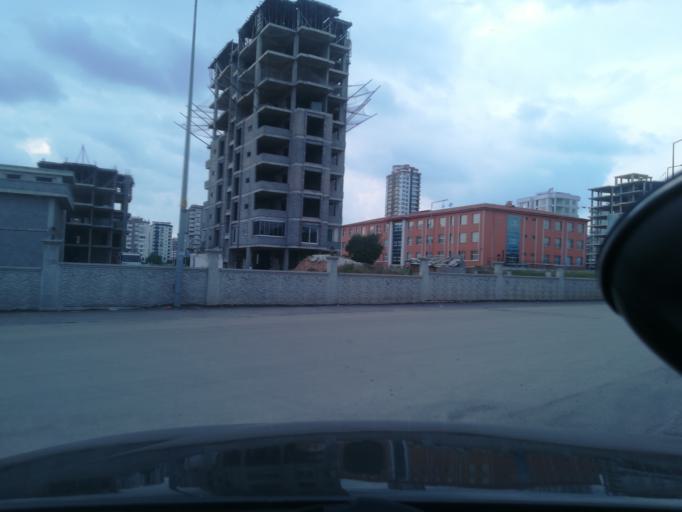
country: TR
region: Adana
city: Seyhan
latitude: 37.0153
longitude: 35.2707
